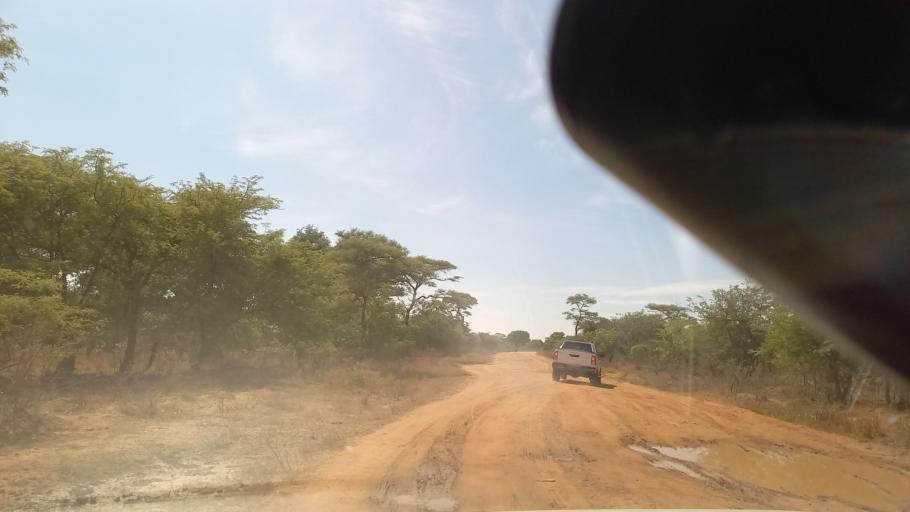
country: ZM
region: Southern
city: Mazabuka
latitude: -16.0327
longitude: 27.6162
